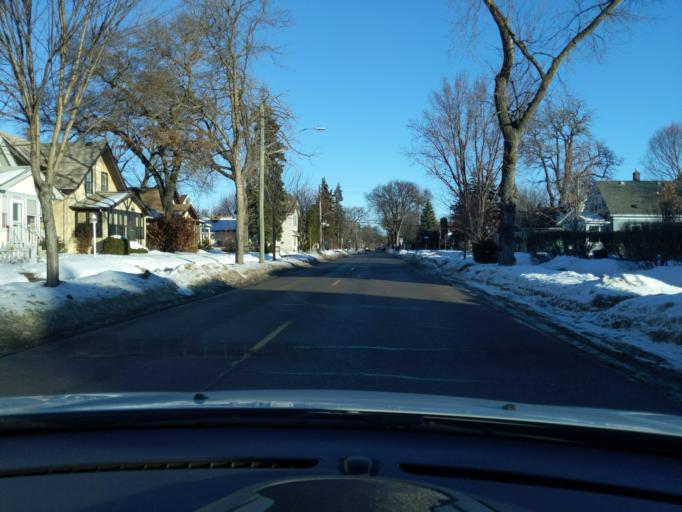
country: US
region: Minnesota
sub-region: Ramsey County
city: Lauderdale
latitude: 44.9443
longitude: -93.2127
